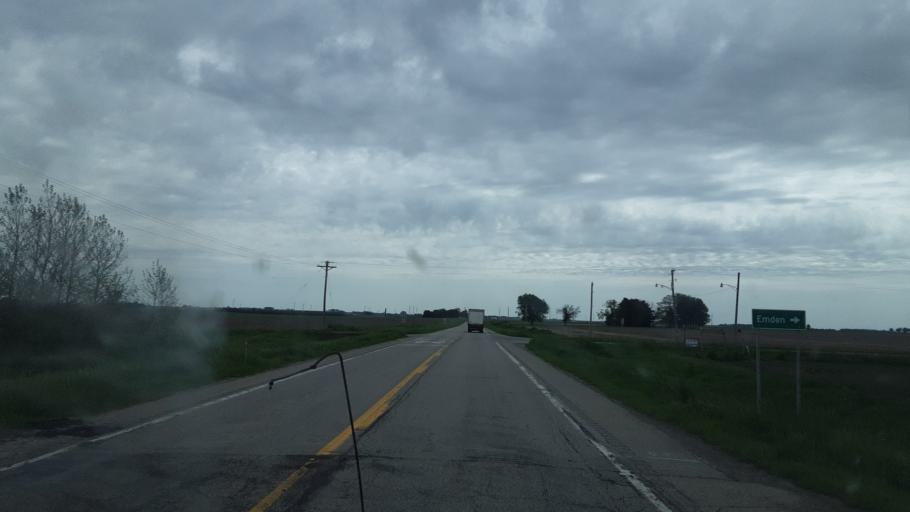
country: US
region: Illinois
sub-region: Tazewell County
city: Delavan
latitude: 40.3075
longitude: -89.4903
